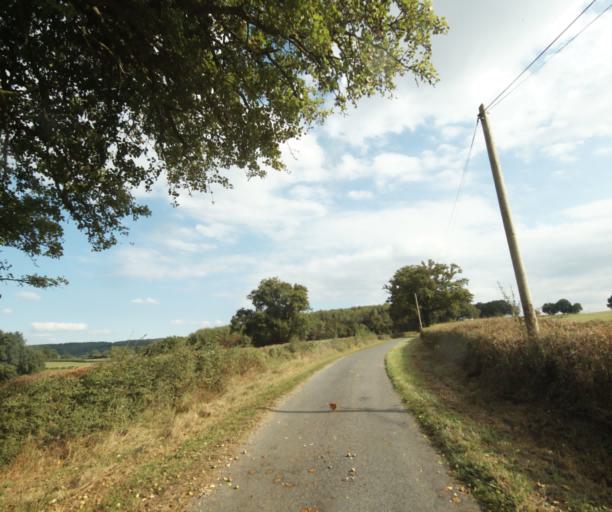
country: FR
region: Bourgogne
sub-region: Departement de Saone-et-Loire
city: Palinges
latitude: 46.5099
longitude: 4.2483
